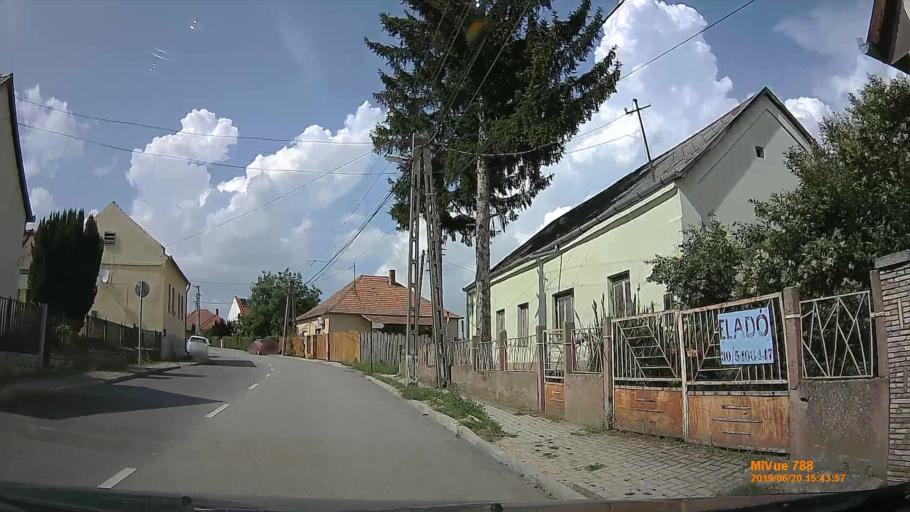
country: HU
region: Baranya
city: Kozarmisleny
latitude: 45.9839
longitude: 18.2608
